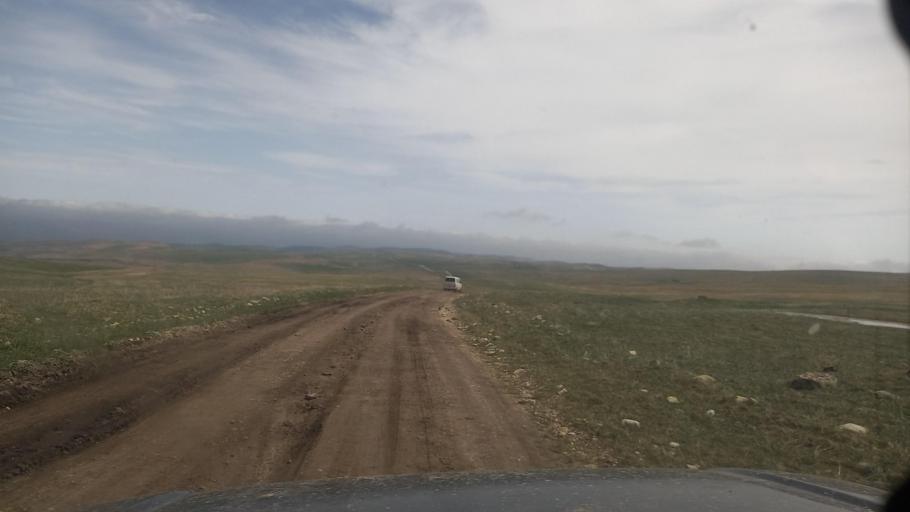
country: RU
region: Stavropol'skiy
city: Kislovodsk
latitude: 43.7578
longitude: 42.7694
